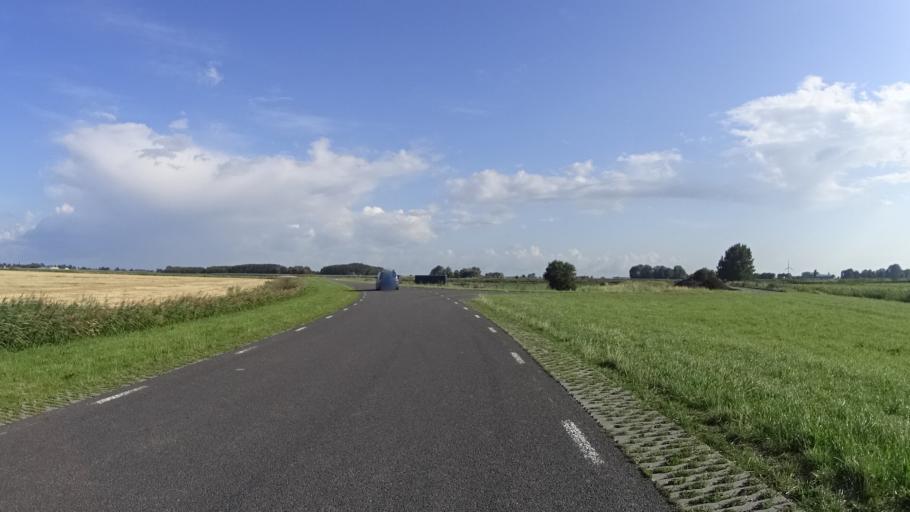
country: NL
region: Friesland
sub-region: Gemeente Harlingen
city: Harlingen
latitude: 53.1273
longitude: 5.4578
